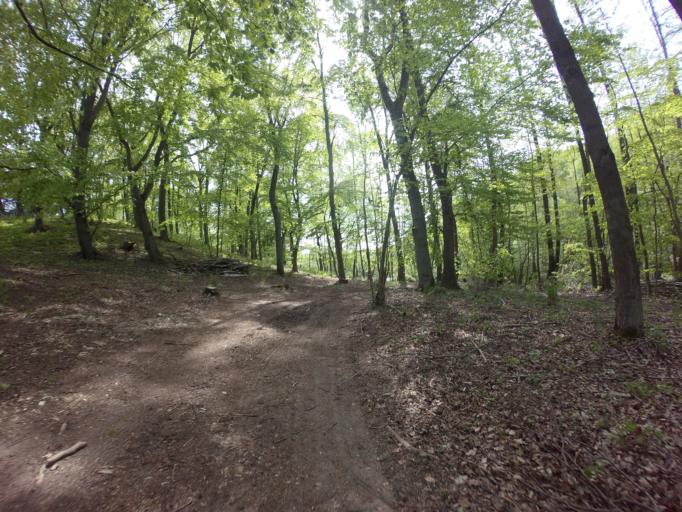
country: PL
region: West Pomeranian Voivodeship
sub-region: Powiat choszczenski
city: Choszczno
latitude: 53.2308
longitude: 15.4146
